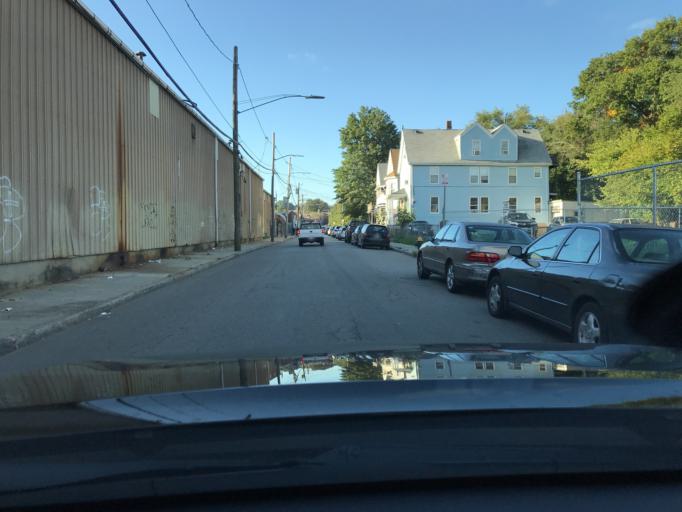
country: US
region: Massachusetts
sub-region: Suffolk County
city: South Boston
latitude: 42.3116
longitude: -71.0722
